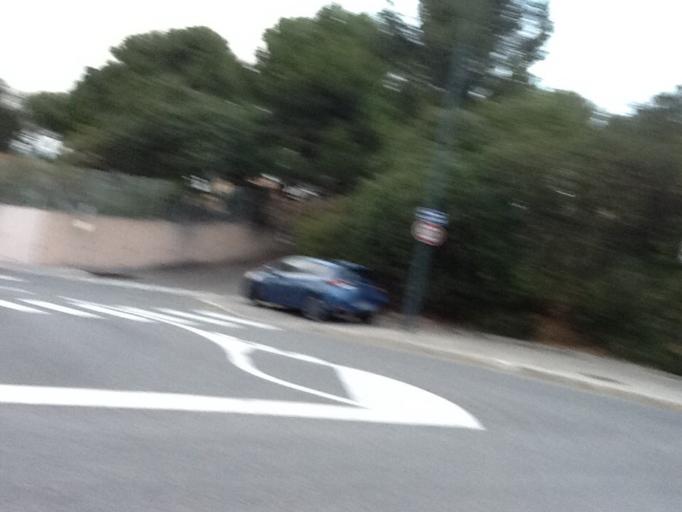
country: FR
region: Provence-Alpes-Cote d'Azur
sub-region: Departement du Var
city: Sanary-sur-Mer
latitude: 43.1139
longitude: 5.8197
